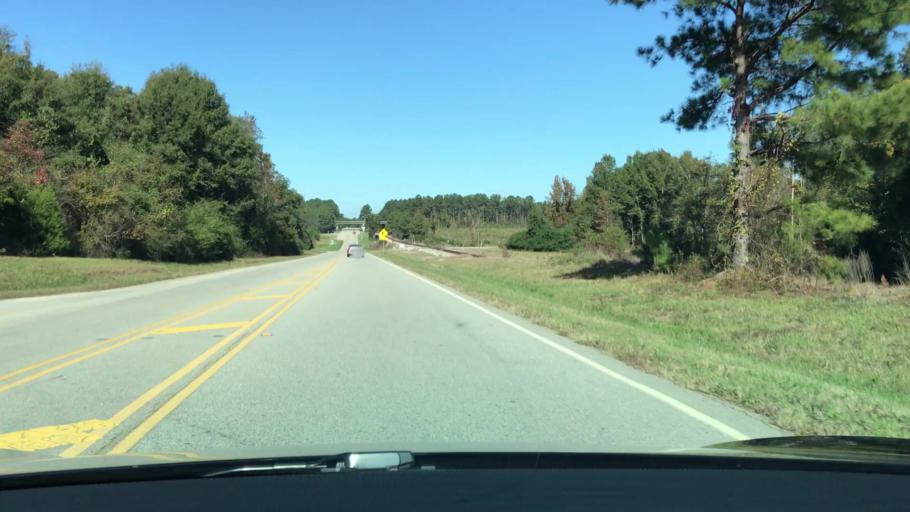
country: US
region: Georgia
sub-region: Taliaferro County
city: Crawfordville
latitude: 33.4926
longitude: -82.7995
